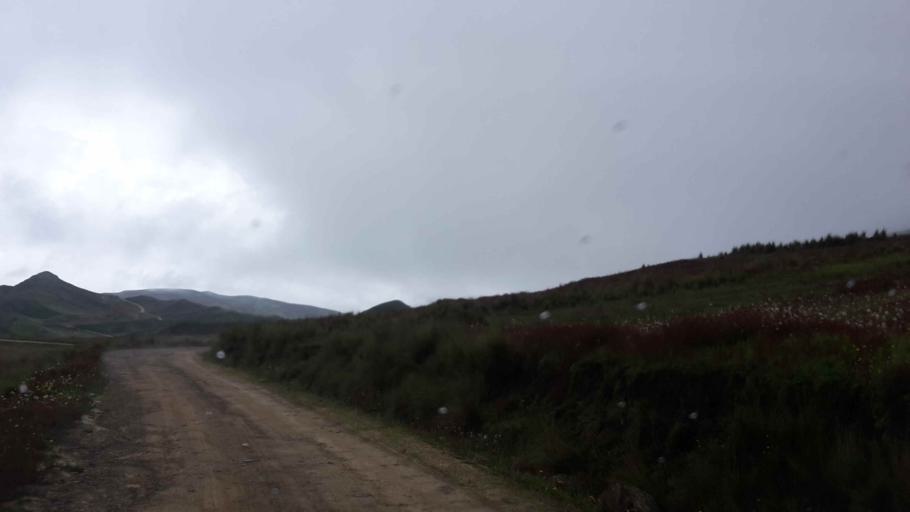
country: BO
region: Cochabamba
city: Cochabamba
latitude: -17.1498
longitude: -66.1038
